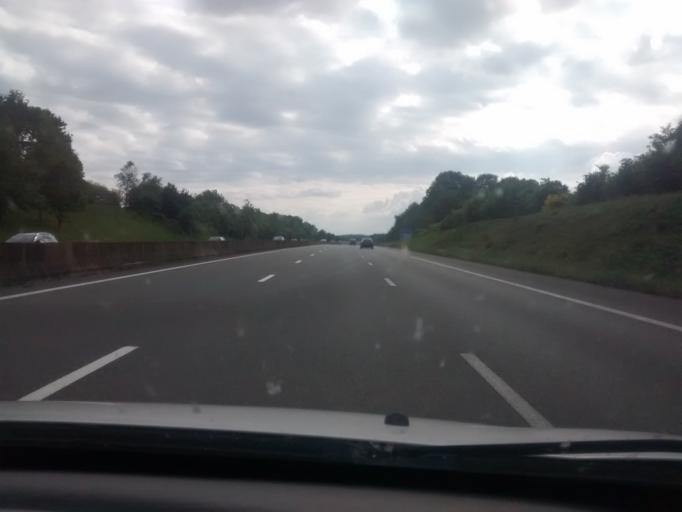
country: FR
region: Centre
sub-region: Departement d'Eure-et-Loir
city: Authon-du-Perche
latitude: 48.2169
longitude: 0.9527
